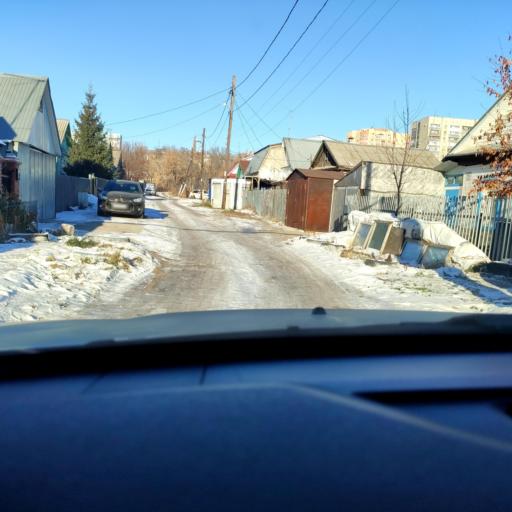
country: RU
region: Samara
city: Samara
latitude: 53.2295
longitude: 50.2259
